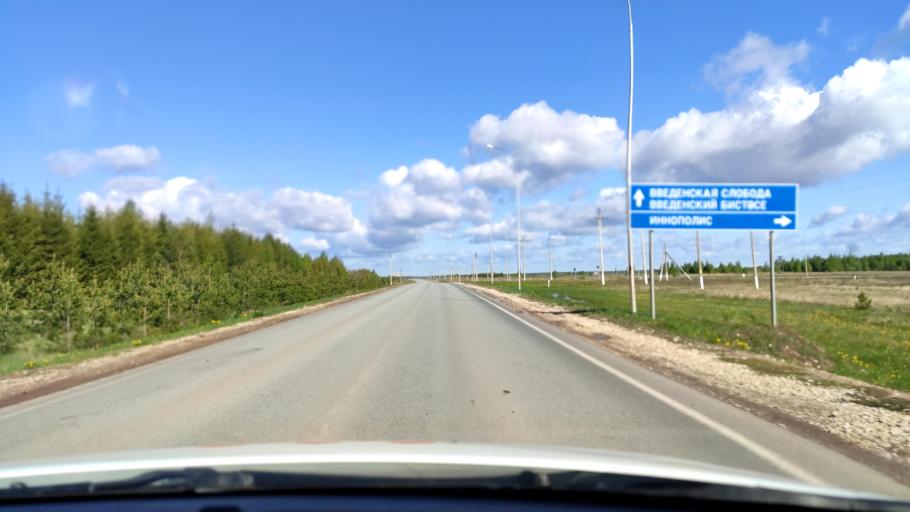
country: RU
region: Tatarstan
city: Sviyazhsk
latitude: 55.7362
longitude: 48.7378
